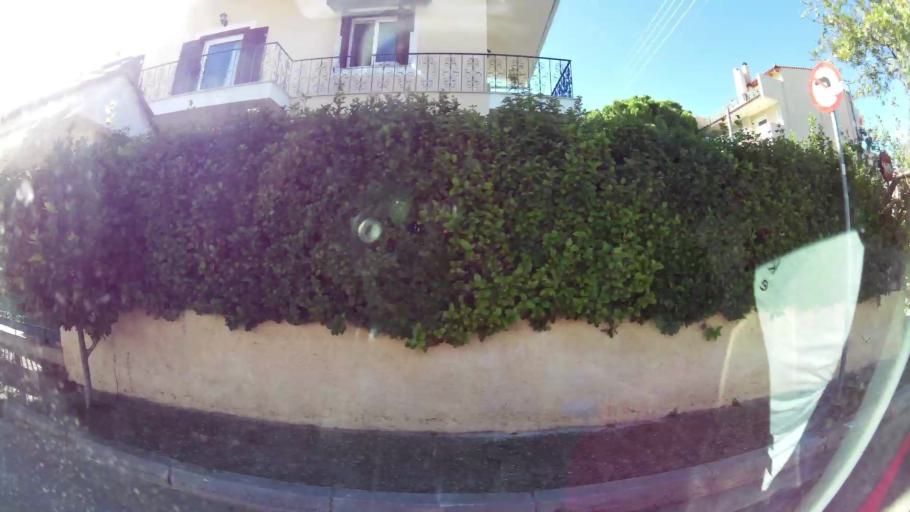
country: GR
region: Attica
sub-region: Nomarchia Anatolikis Attikis
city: Leondarion
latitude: 37.9809
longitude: 23.8590
